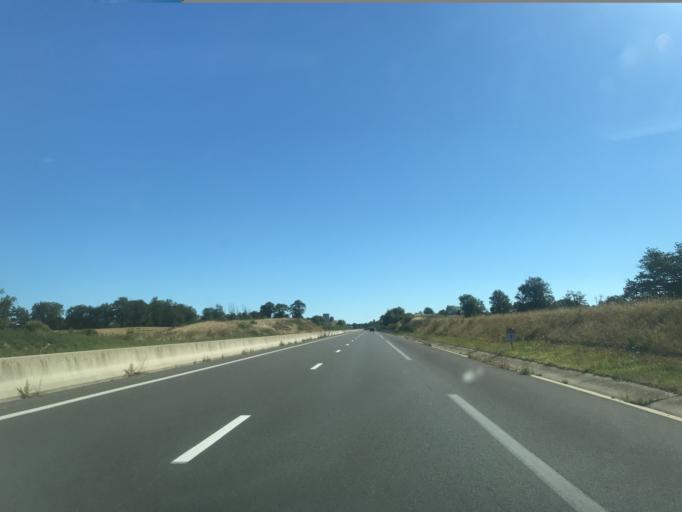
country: FR
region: Auvergne
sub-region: Departement de l'Allier
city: Huriel
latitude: 46.2935
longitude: 2.4227
